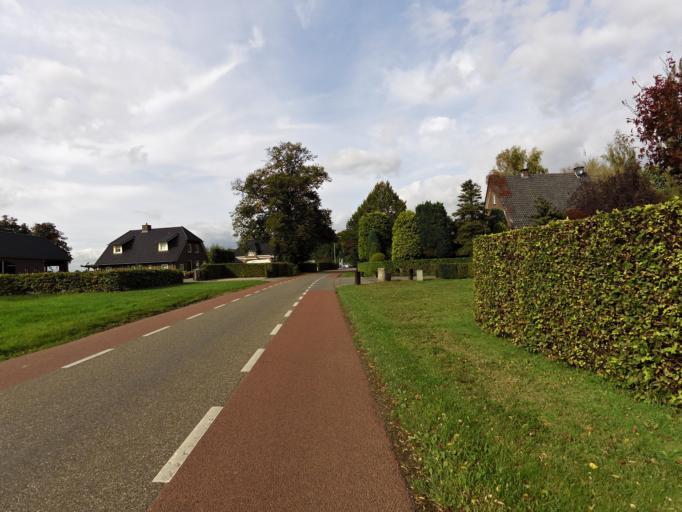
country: NL
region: Gelderland
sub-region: Gemeente Bronckhorst
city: Baak
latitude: 52.0747
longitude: 6.2684
